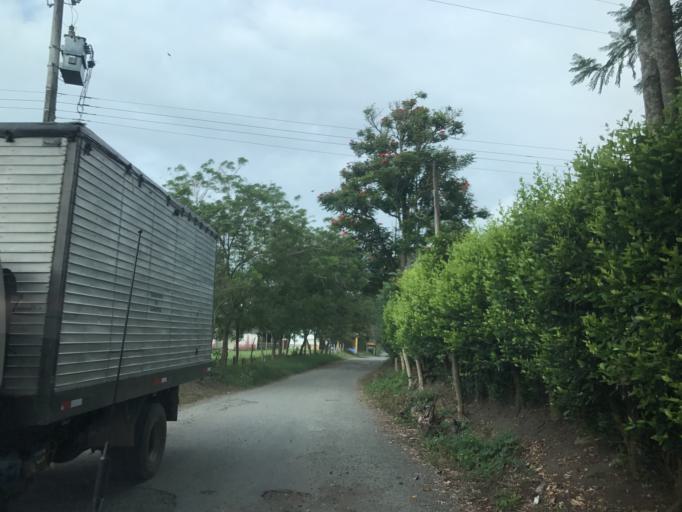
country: CO
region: Quindio
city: Montenegro
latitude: 4.5409
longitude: -75.8542
